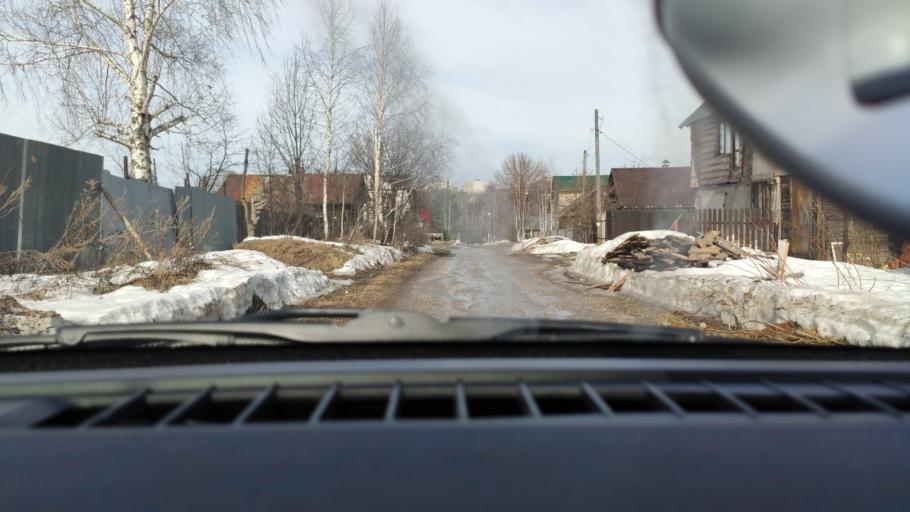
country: RU
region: Perm
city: Perm
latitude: 58.0204
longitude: 56.3189
